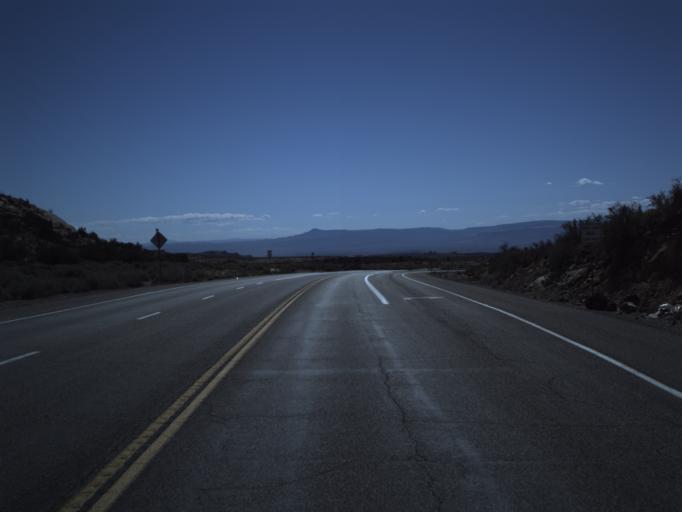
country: US
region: Utah
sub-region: Washington County
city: Ivins
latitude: 37.2323
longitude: -113.6342
